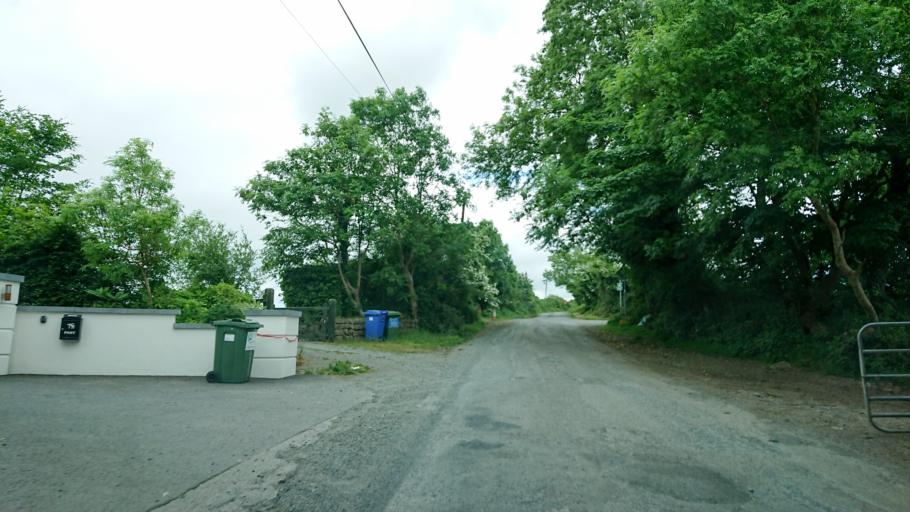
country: IE
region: Munster
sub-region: Waterford
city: Waterford
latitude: 52.2429
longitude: -7.0192
